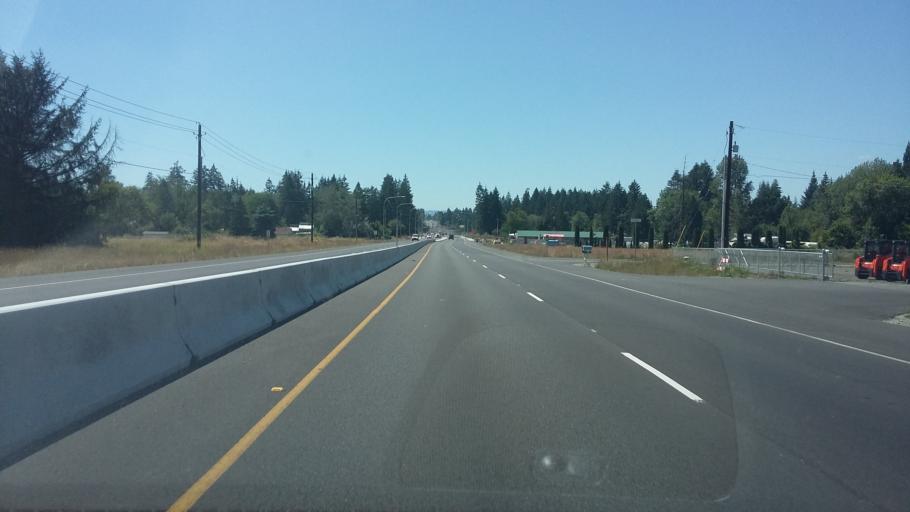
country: US
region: Washington
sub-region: Clark County
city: Dollar Corner
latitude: 45.7803
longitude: -122.5913
